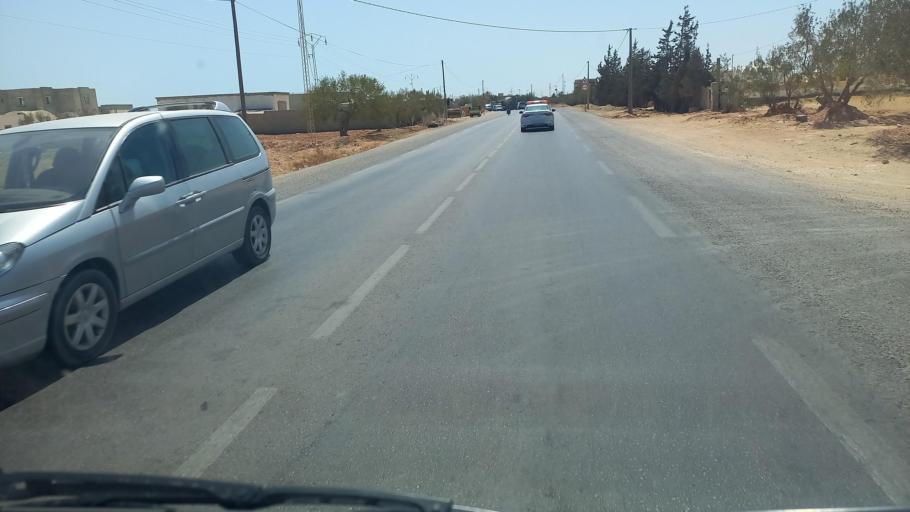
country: TN
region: Madanin
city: Houmt Souk
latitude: 33.8170
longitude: 10.8733
